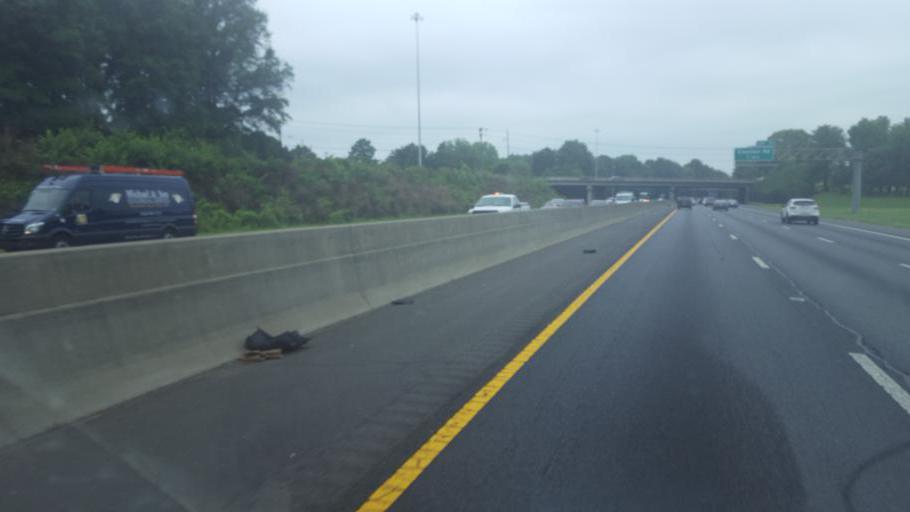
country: US
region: North Carolina
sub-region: Mecklenburg County
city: Charlotte
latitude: 35.1808
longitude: -80.8869
